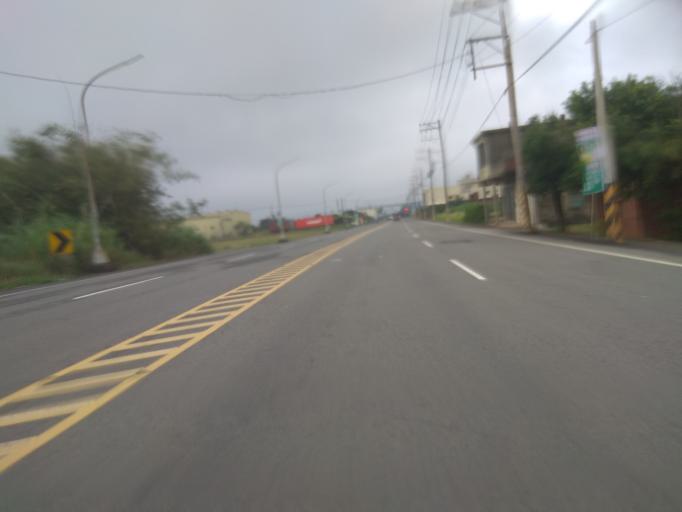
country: TW
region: Taiwan
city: Taoyuan City
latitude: 25.0323
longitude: 121.0983
